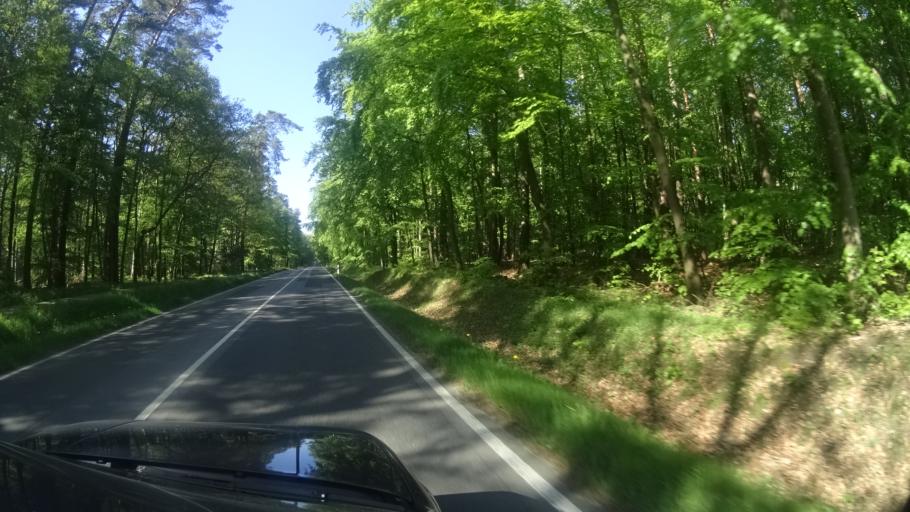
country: DE
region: Mecklenburg-Vorpommern
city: Rovershagen
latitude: 54.2034
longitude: 12.2122
